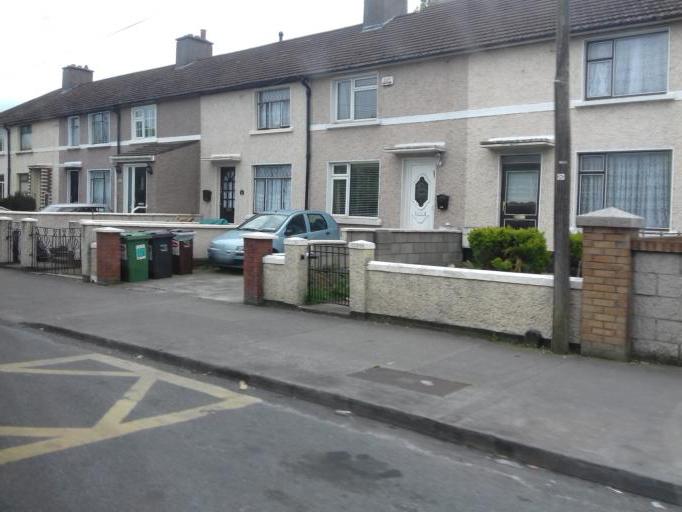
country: IE
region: Leinster
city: Chapelizod
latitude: 53.3425
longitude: -6.3465
